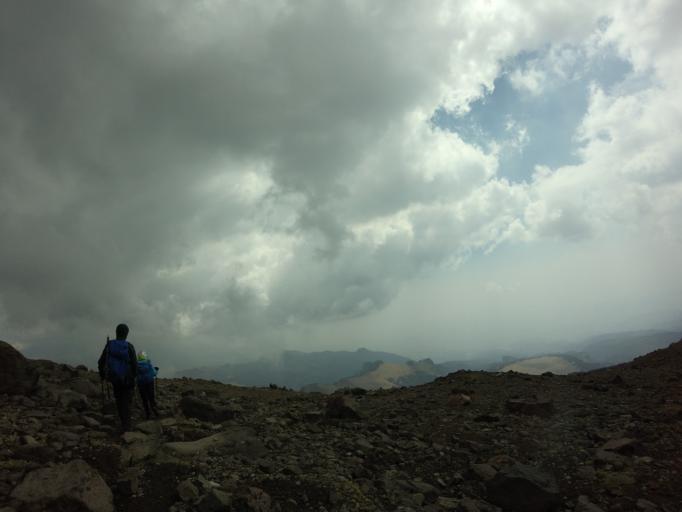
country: MX
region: Mexico
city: Amecameca de Juarez
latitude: 19.1620
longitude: -98.6455
